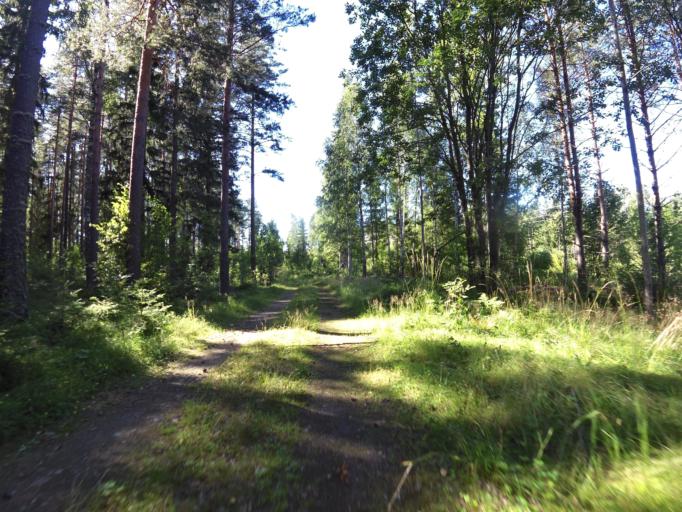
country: SE
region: Gaevleborg
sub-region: Hofors Kommun
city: Hofors
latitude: 60.5663
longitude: 16.4718
